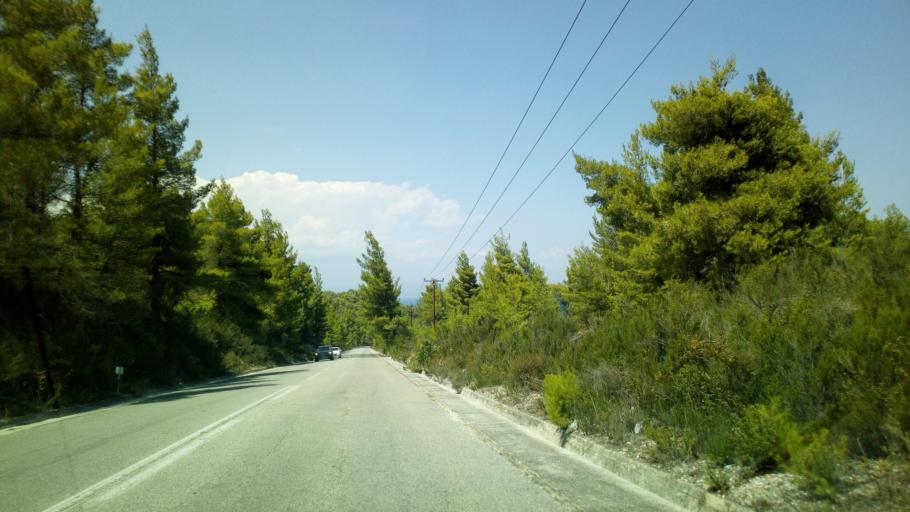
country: GR
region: Central Macedonia
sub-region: Nomos Chalkidikis
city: Sarti
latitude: 40.1435
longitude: 23.9218
